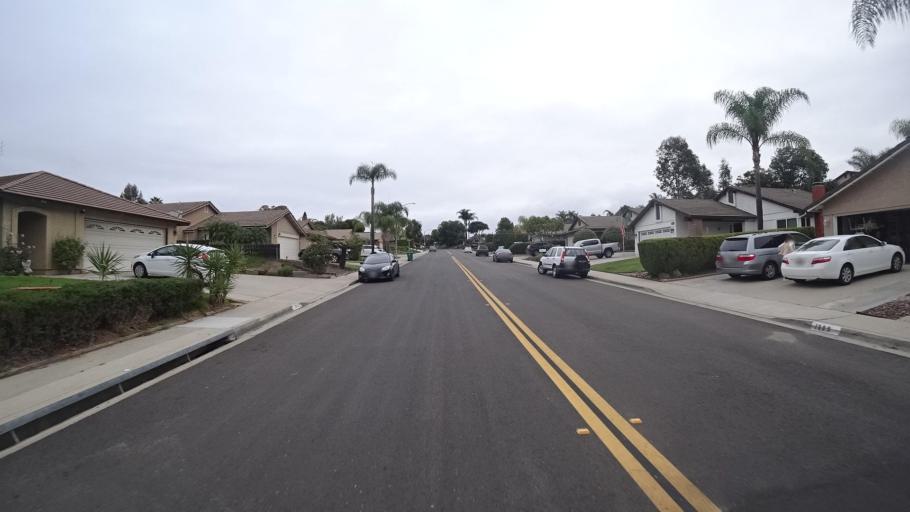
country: US
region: California
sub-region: San Diego County
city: Rancho San Diego
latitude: 32.7563
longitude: -116.9148
